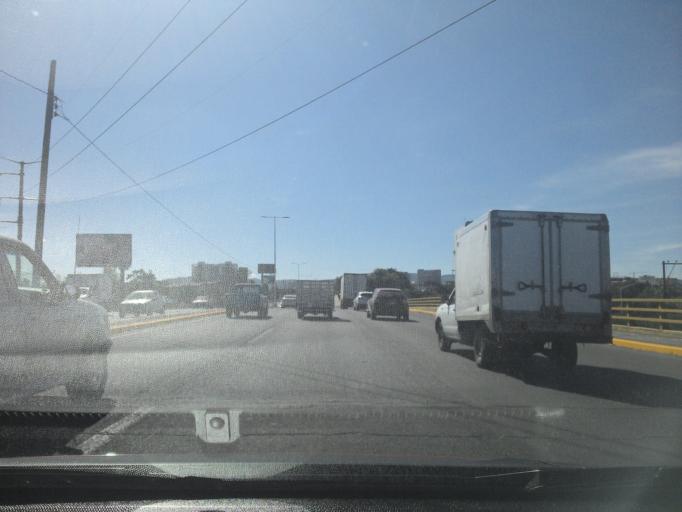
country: MX
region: Jalisco
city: Zapopan2
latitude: 20.7315
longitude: -103.4118
